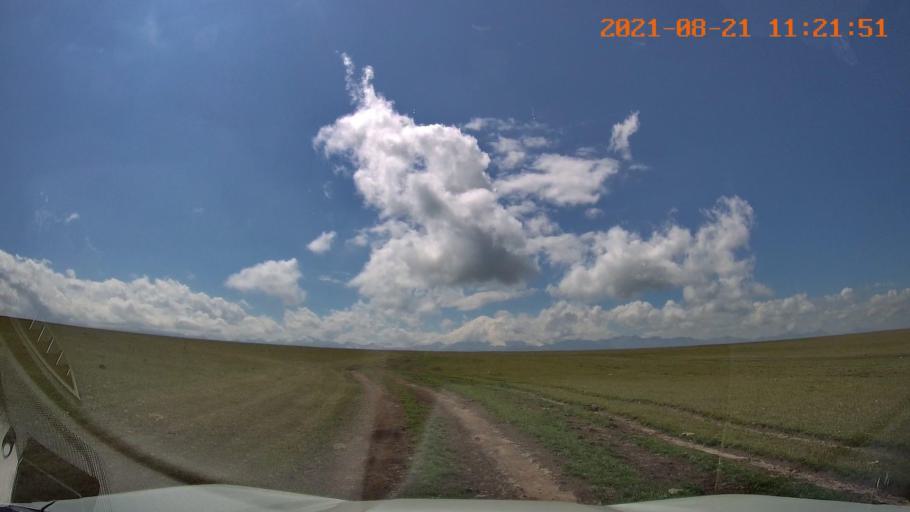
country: RU
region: Stavropol'skiy
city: Kislovodsk
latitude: 43.6170
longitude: 42.5923
